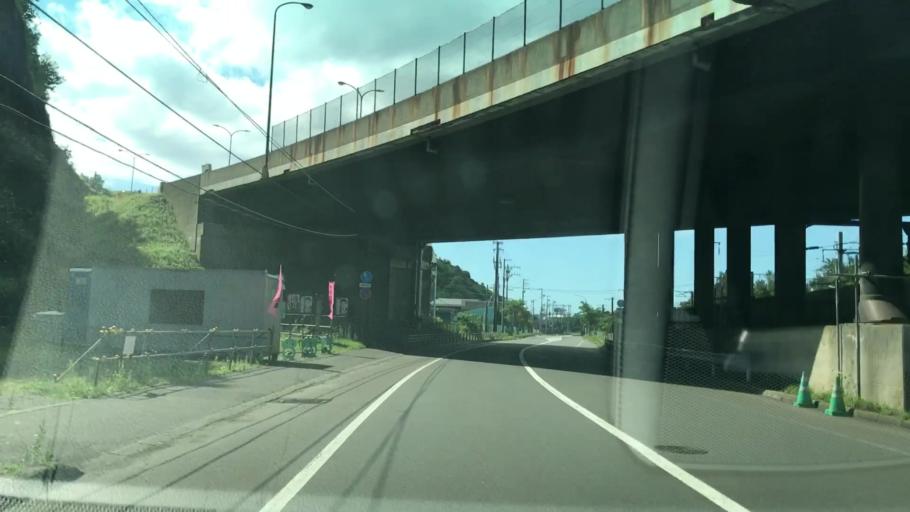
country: JP
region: Hokkaido
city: Muroran
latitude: 42.3336
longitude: 141.0030
